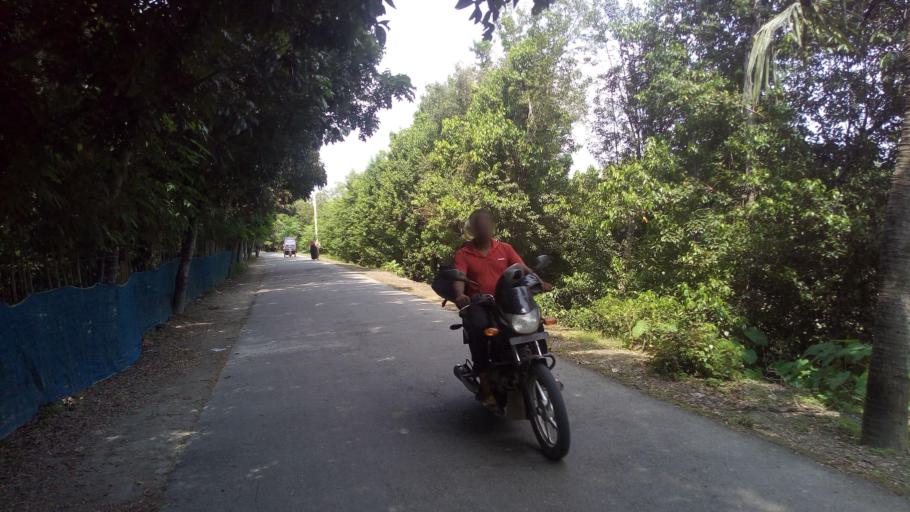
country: BD
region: Khulna
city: Phultala
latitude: 22.5760
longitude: 89.4523
